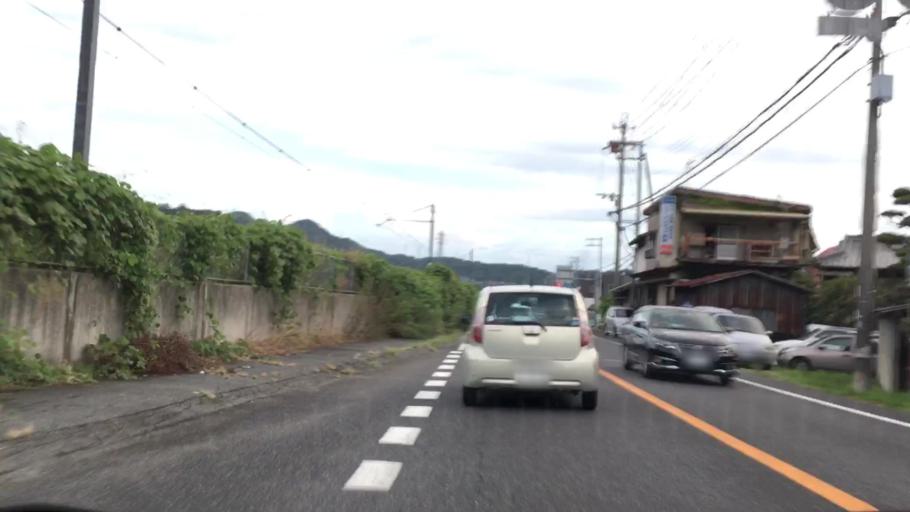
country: JP
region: Hyogo
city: Himeji
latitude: 34.8751
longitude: 134.7295
